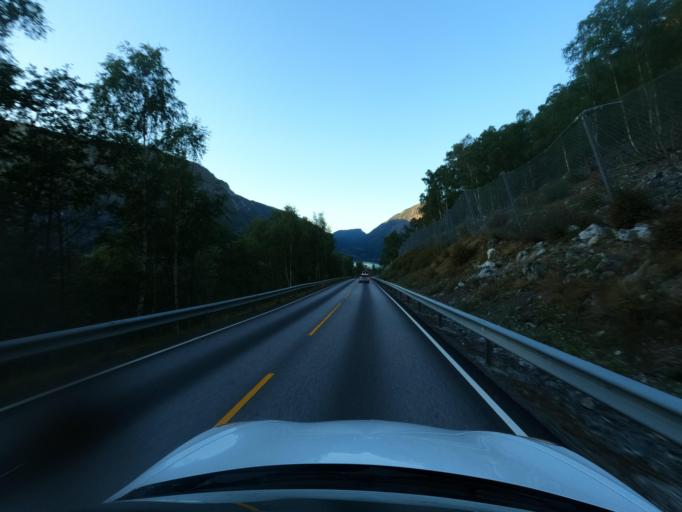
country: NO
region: Sogn og Fjordane
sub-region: Ardal
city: Ardalstangen
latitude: 61.1964
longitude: 7.6281
